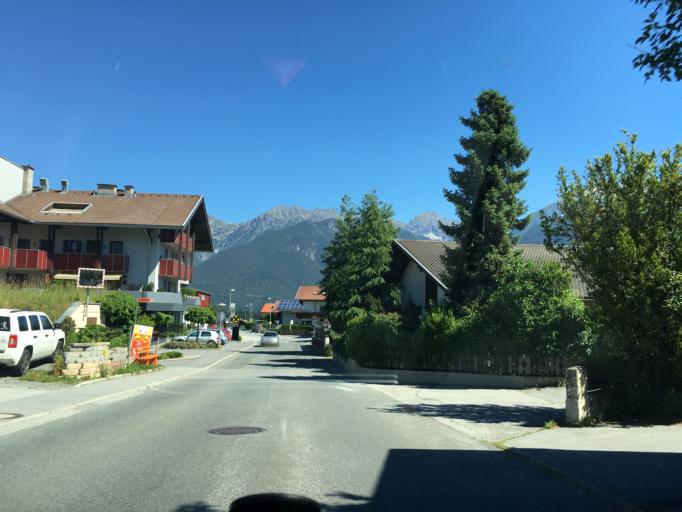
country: AT
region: Tyrol
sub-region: Politischer Bezirk Innsbruck Land
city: Oberperfuss
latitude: 47.2439
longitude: 11.2478
